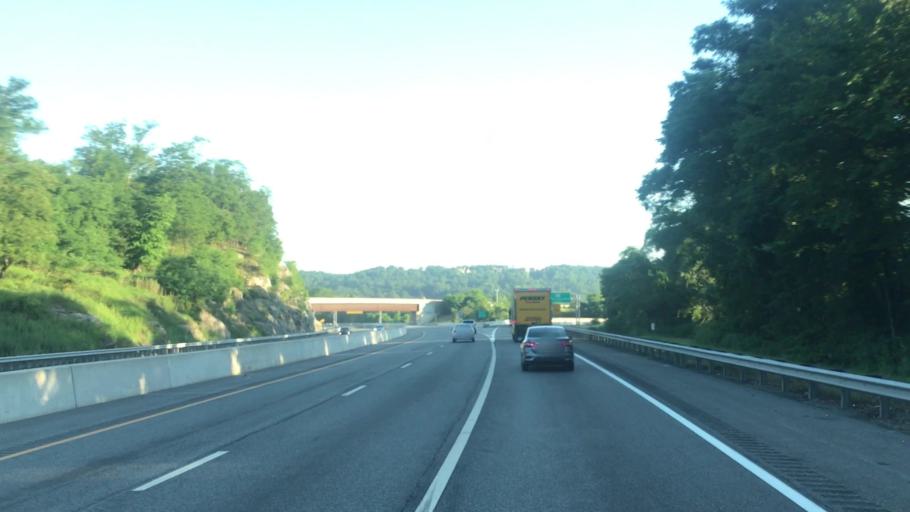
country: US
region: New York
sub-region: Westchester County
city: Elmsford
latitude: 41.0541
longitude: -73.8337
